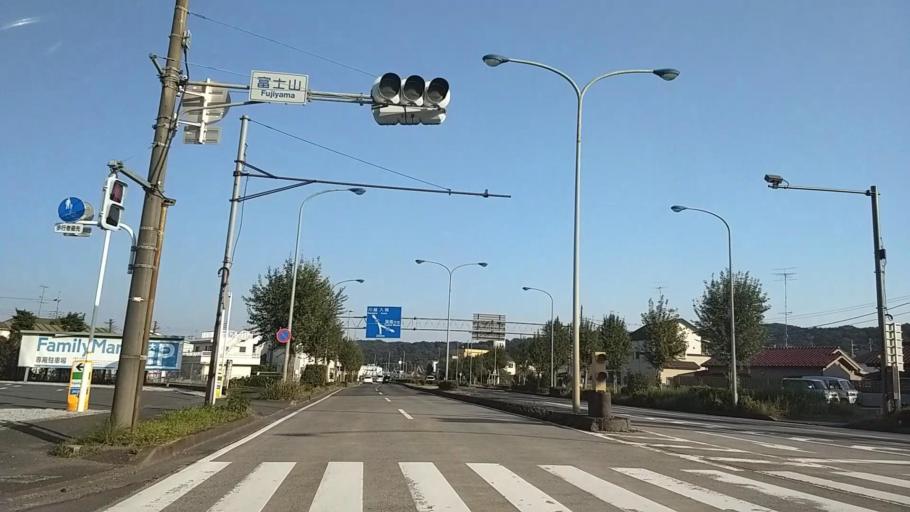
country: JP
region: Tokyo
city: Fussa
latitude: 35.7847
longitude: 139.3542
